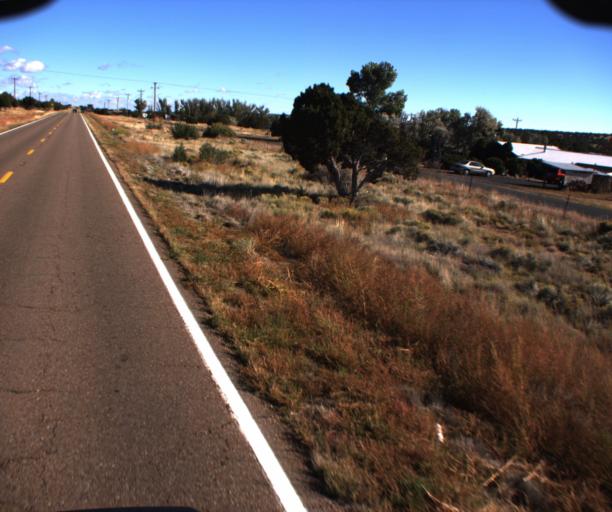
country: US
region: Arizona
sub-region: Apache County
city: Saint Johns
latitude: 34.4318
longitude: -109.6379
